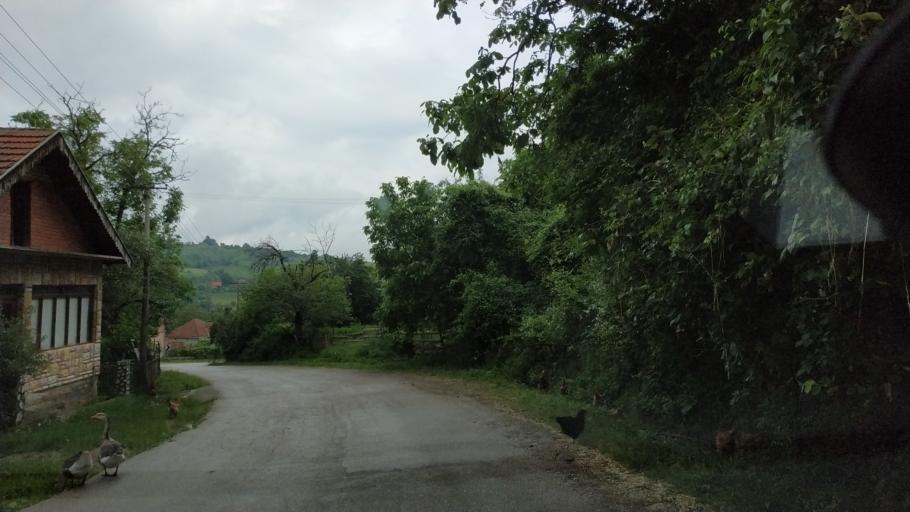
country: RS
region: Central Serbia
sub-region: Toplicki Okrug
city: Prokuplje
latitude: 43.3959
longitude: 21.5547
